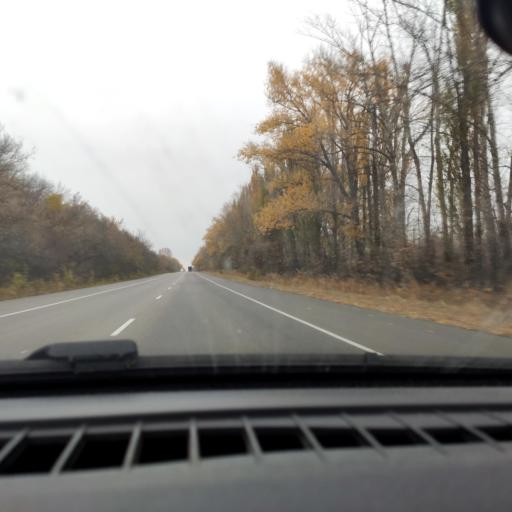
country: RU
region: Voronezj
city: Uryv-Pokrovka
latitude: 51.1615
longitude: 39.0689
